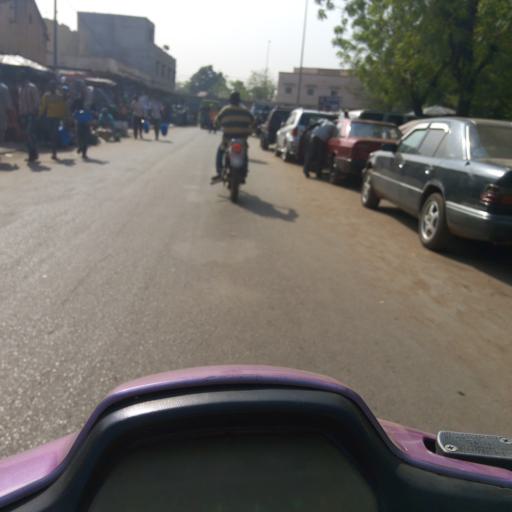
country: ML
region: Bamako
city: Bamako
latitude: 12.6470
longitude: -7.9925
